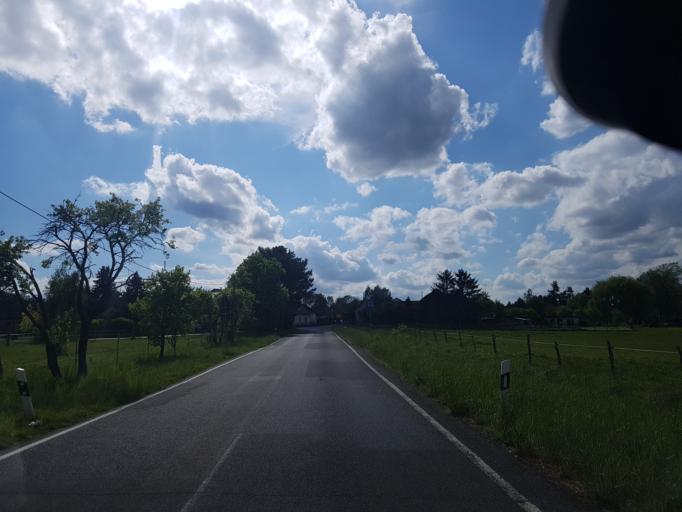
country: DE
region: Brandenburg
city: Cottbus
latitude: 51.6779
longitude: 14.3656
